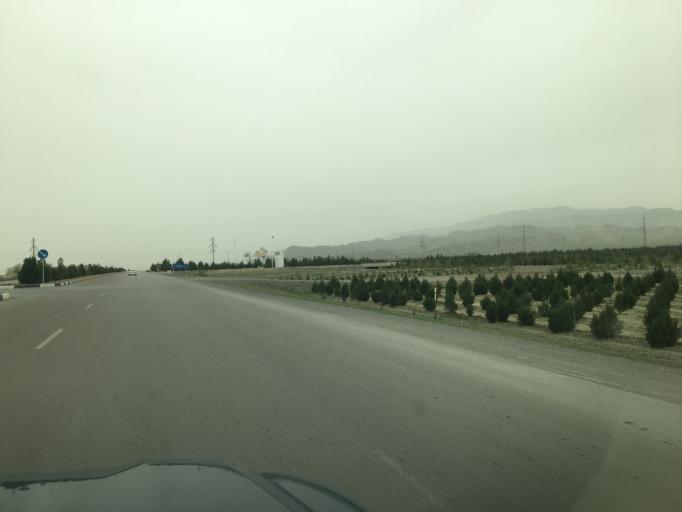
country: TM
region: Ahal
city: Baharly
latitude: 38.2847
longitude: 57.6612
